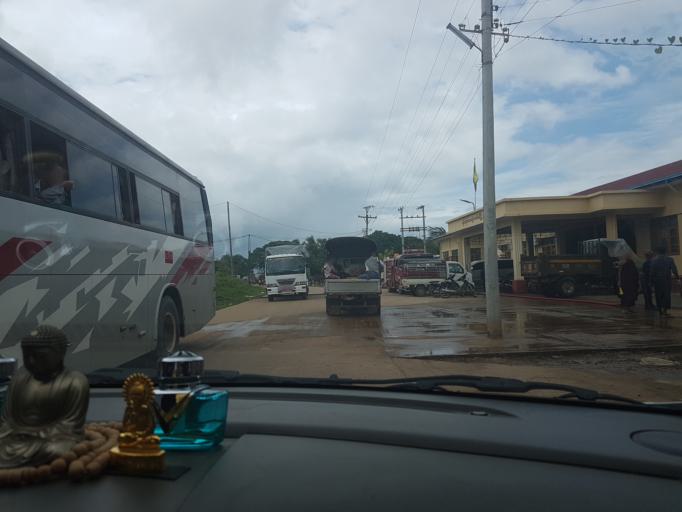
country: MM
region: Bago
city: Nyaunglebin
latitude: 17.9144
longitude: 96.8433
